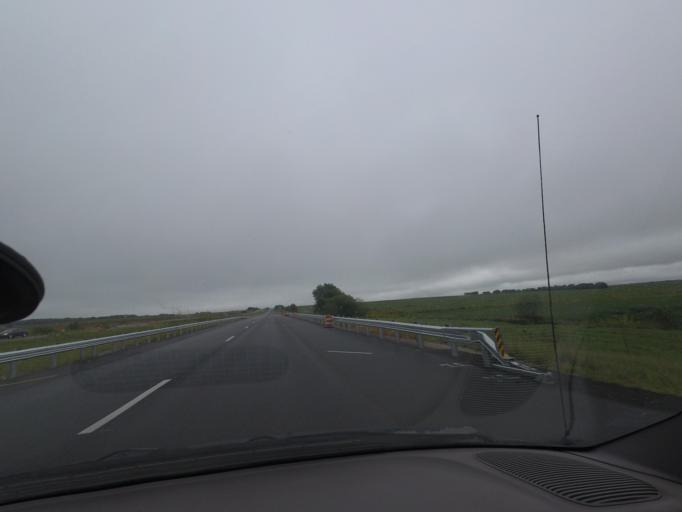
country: US
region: Illinois
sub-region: Macon County
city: Harristown
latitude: 39.8314
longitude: -89.1014
